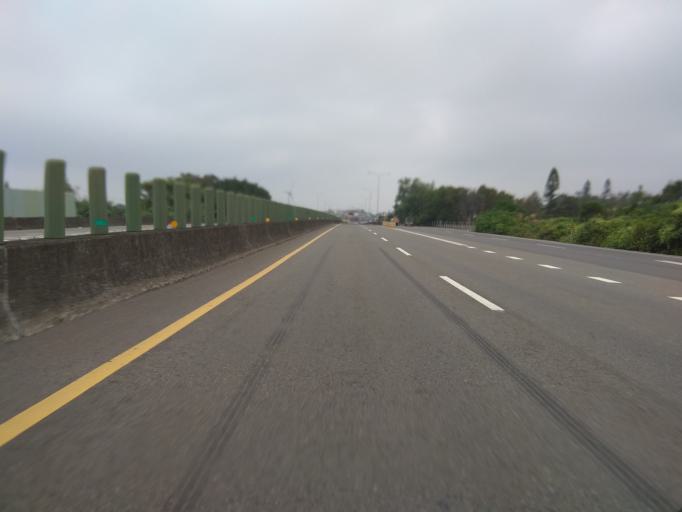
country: TW
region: Taiwan
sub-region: Hsinchu
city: Hsinchu
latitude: 24.7083
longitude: 120.8674
